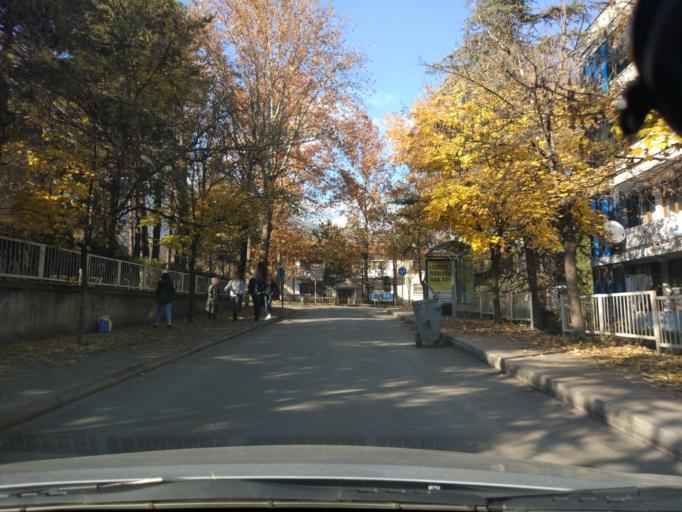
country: TR
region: Karabuk
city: Karabuk
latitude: 41.2013
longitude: 32.6217
